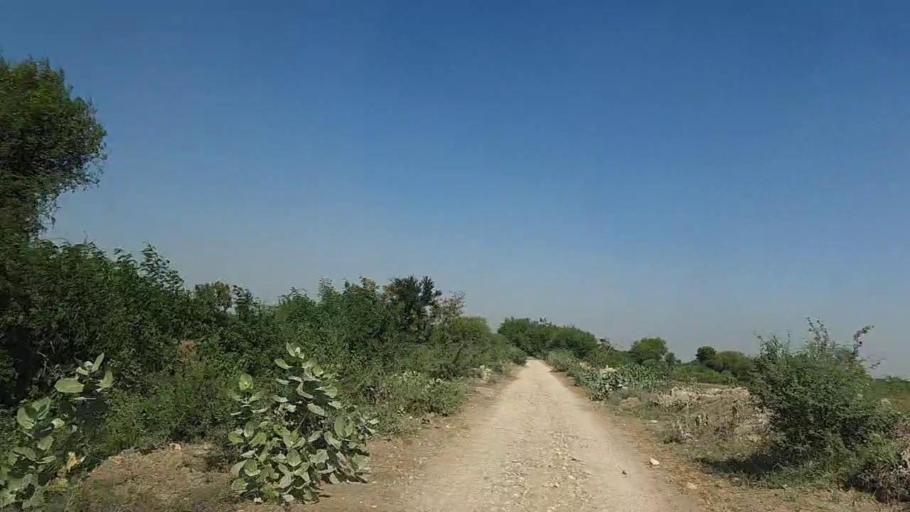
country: PK
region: Sindh
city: Daro Mehar
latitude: 24.7523
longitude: 68.1585
